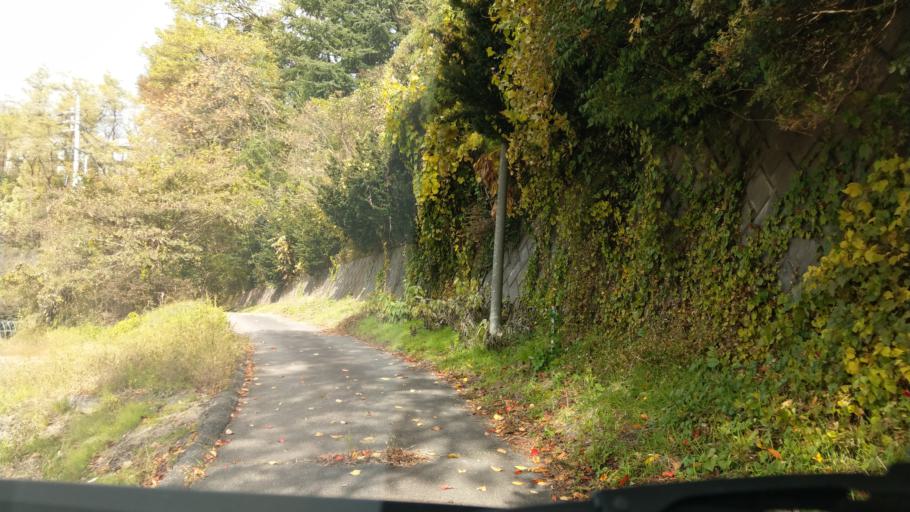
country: JP
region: Nagano
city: Komoro
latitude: 36.3294
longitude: 138.4140
